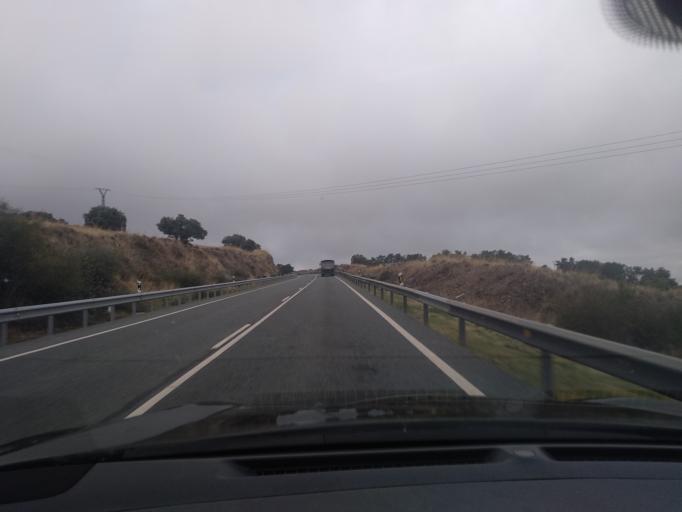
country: ES
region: Castille and Leon
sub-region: Provincia de Segovia
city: Otero de Herreros
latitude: 40.7983
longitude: -4.2132
